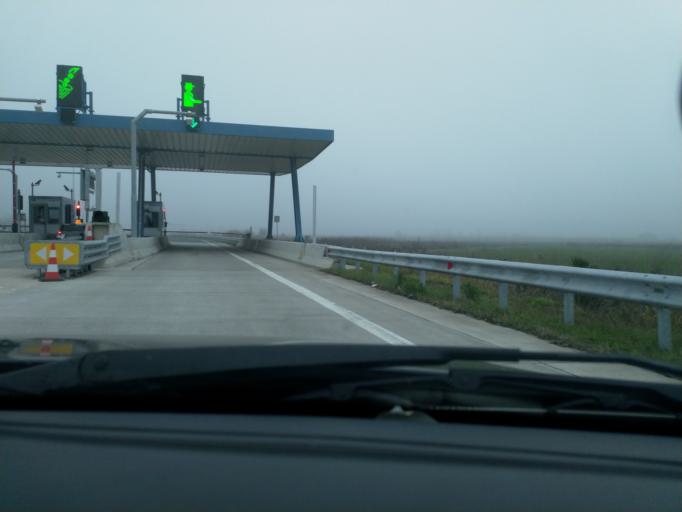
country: GR
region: Thessaly
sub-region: Nomos Kardhitsas
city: Anavra
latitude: 39.2567
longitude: 22.0832
